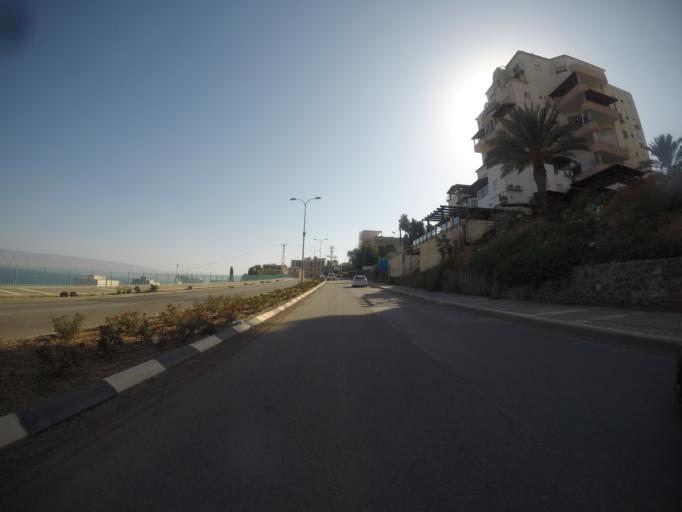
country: IL
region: Northern District
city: Tiberias
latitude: 32.7944
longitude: 35.5395
